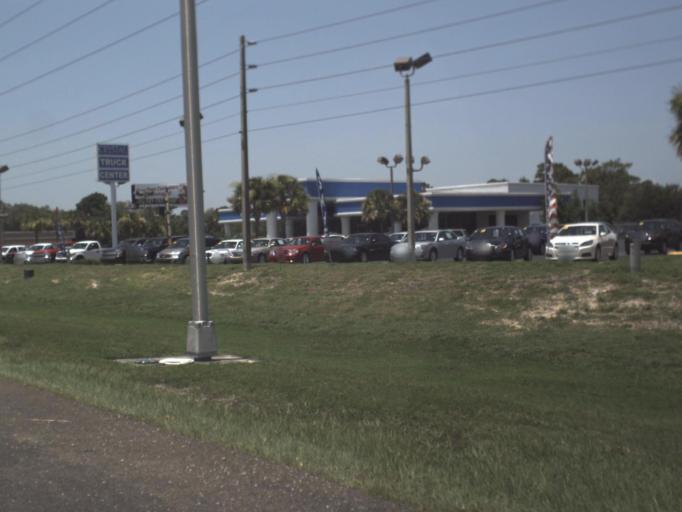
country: US
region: Florida
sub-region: Hernando County
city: Timber Pines
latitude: 28.4841
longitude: -82.6061
